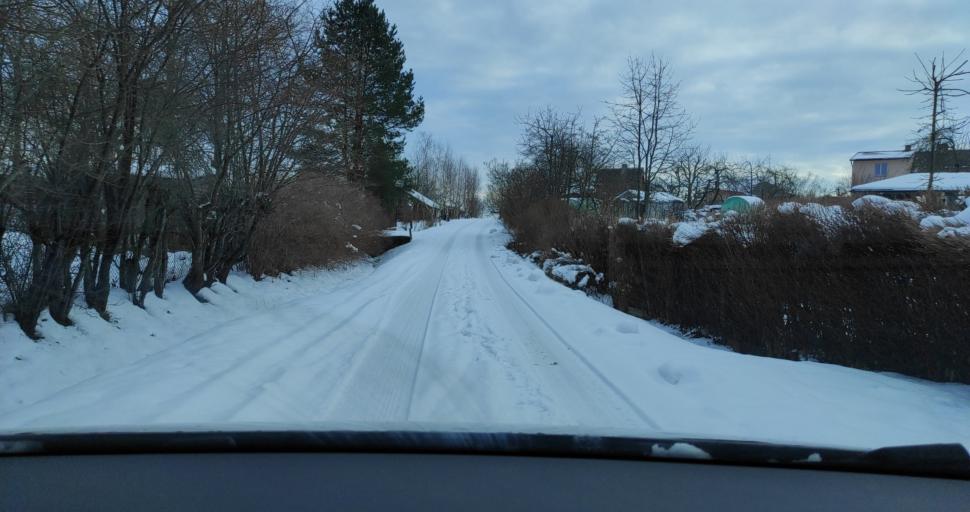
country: LV
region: Kuldigas Rajons
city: Kuldiga
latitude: 56.9438
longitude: 22.0058
